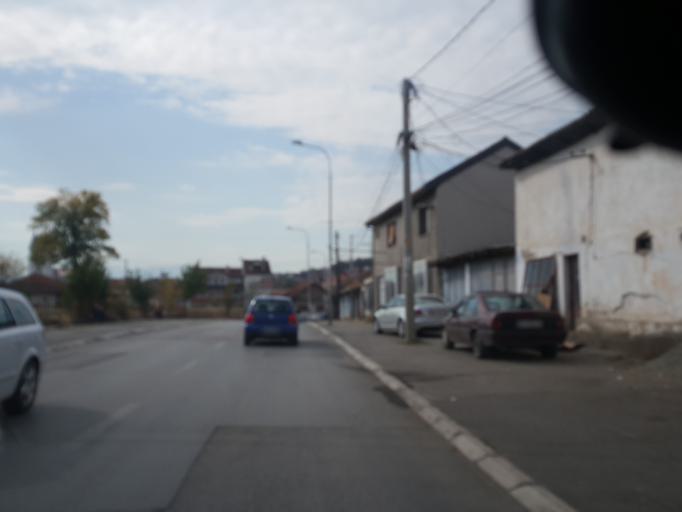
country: XK
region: Gjakova
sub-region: Komuna e Gjakoves
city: Gjakove
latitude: 42.3749
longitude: 20.4311
